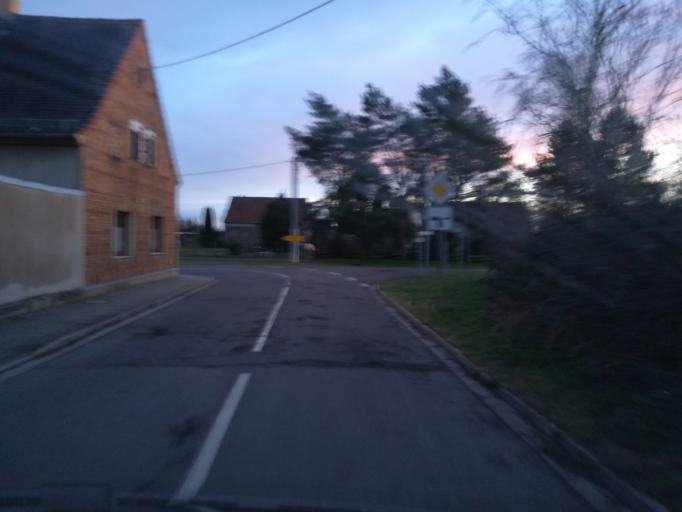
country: DE
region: Saxony-Anhalt
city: Roitzsch
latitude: 51.5509
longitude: 12.2734
